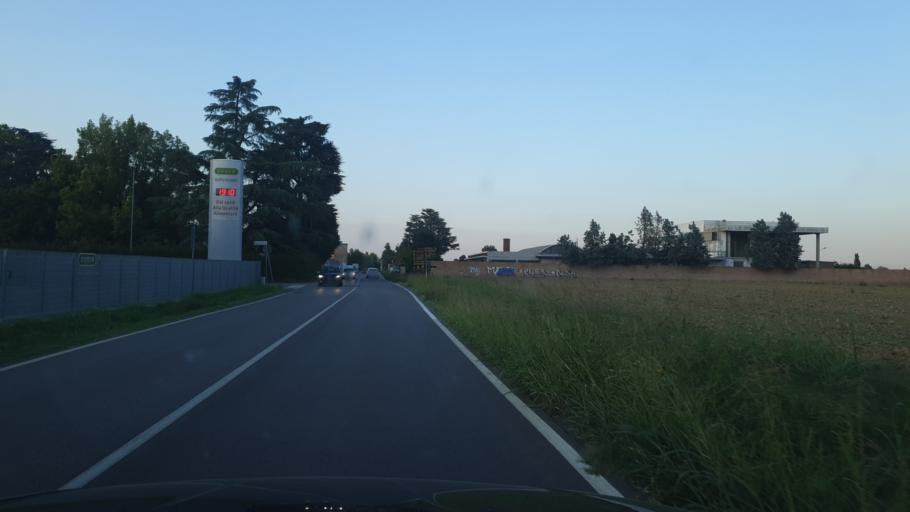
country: IT
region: Emilia-Romagna
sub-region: Provincia di Bologna
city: Quarto Inferiore
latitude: 44.5420
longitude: 11.3948
